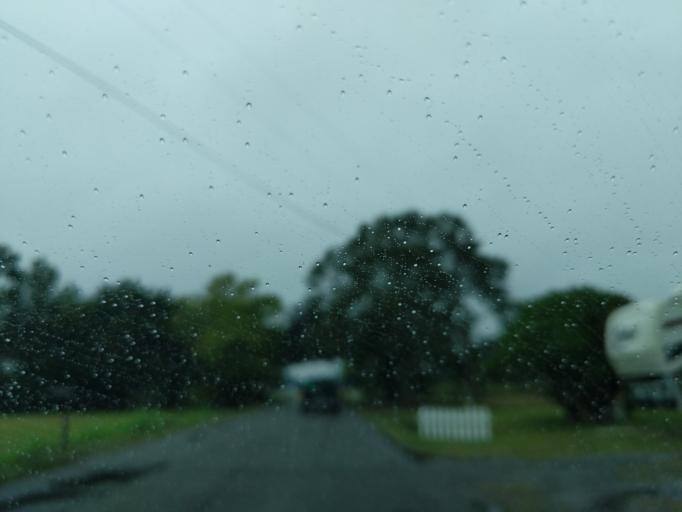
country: US
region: Louisiana
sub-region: Vermilion Parish
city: Kaplan
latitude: 29.9932
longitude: -92.2826
